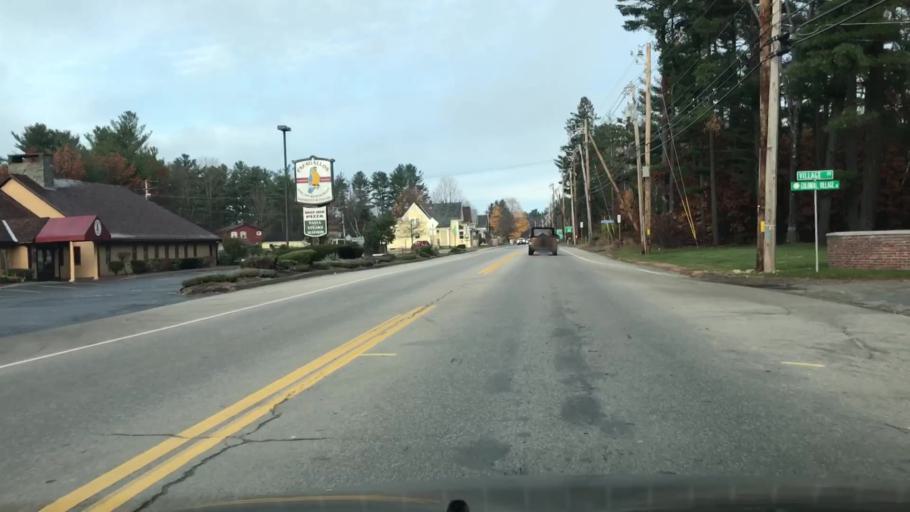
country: US
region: New Hampshire
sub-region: Cheshire County
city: Keene
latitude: 42.9106
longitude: -72.2627
